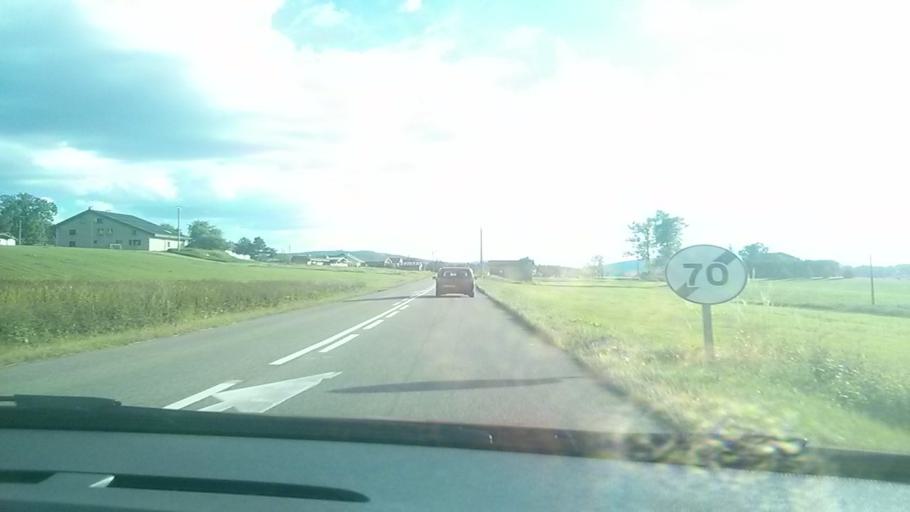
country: FR
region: Franche-Comte
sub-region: Departement du Jura
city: Les Rousses
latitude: 46.4980
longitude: 6.0983
